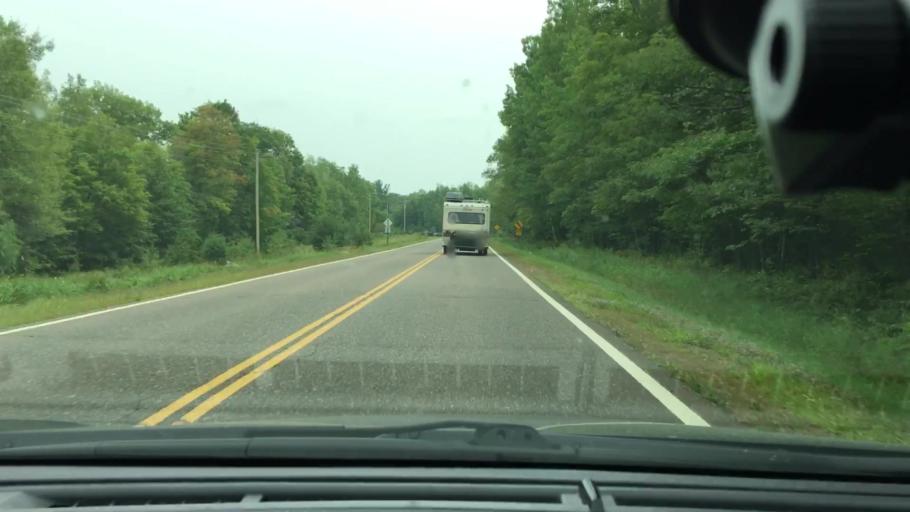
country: US
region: Minnesota
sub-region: Aitkin County
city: Aitkin
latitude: 46.4021
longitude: -93.7980
